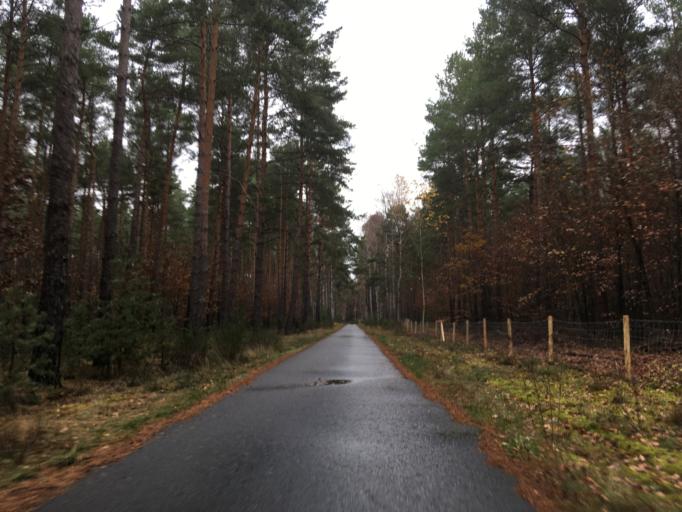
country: DE
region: Brandenburg
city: Jamlitz
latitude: 52.0529
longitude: 14.4803
